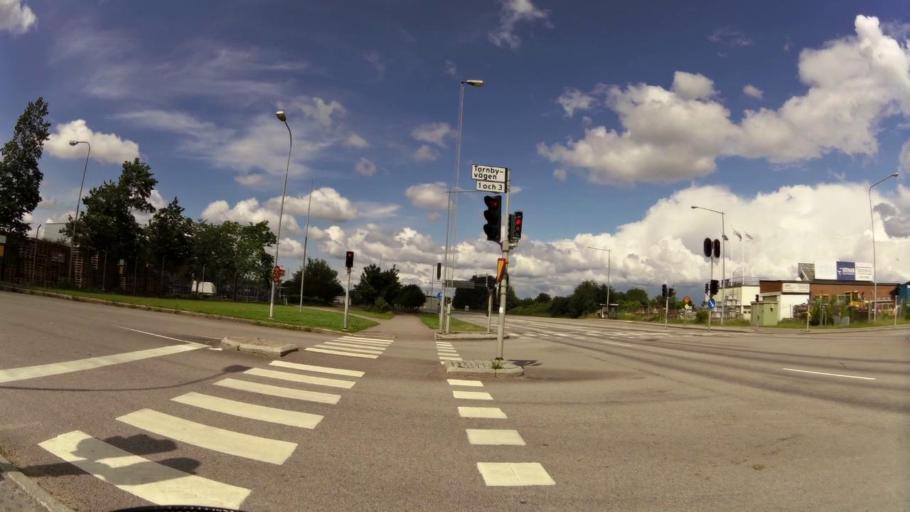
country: SE
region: OEstergoetland
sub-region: Linkopings Kommun
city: Linkoping
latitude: 58.4243
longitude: 15.6152
